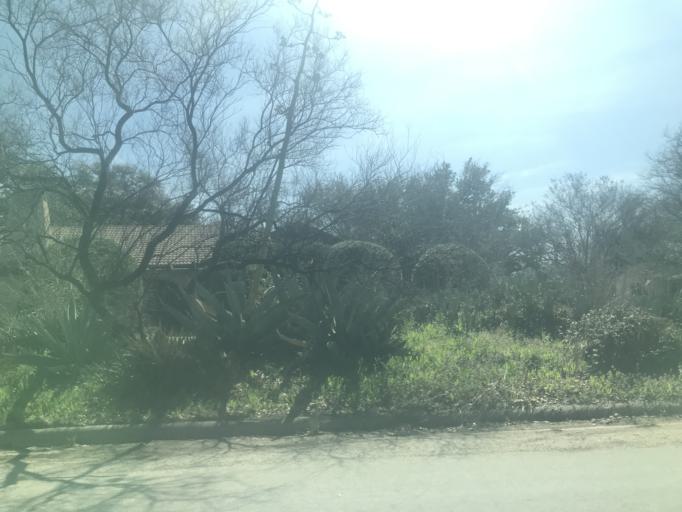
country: US
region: Texas
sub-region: Taylor County
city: Abilene
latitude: 32.4409
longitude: -99.7749
